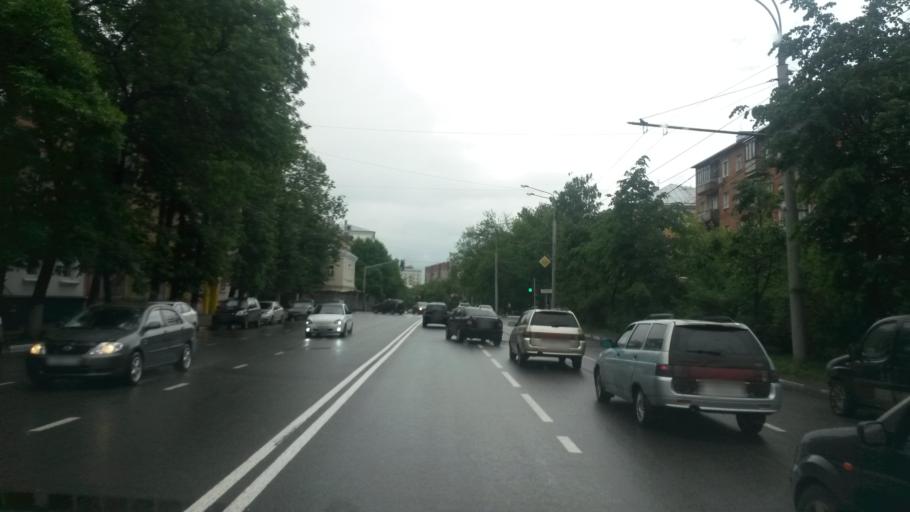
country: RU
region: Jaroslavl
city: Yaroslavl
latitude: 57.6288
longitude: 39.8584
